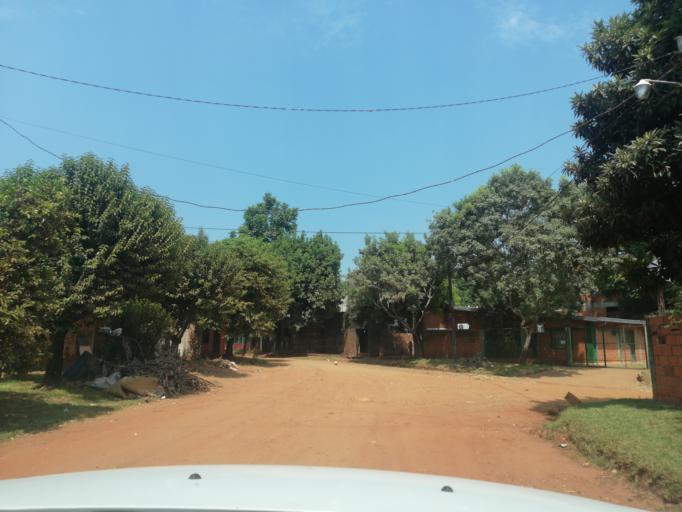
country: AR
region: Misiones
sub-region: Departamento de Capital
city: Posadas
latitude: -27.4365
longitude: -55.8851
